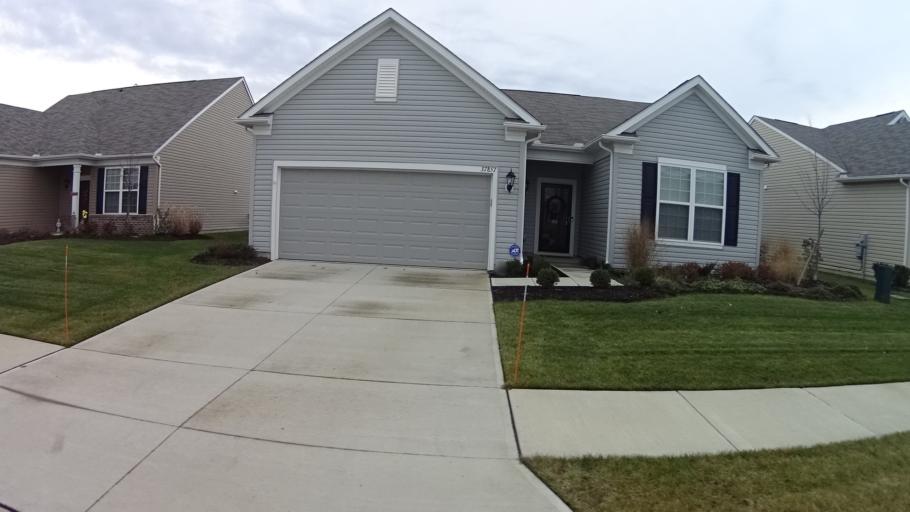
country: US
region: Ohio
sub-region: Lorain County
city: North Ridgeville
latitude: 41.3522
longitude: -82.0455
